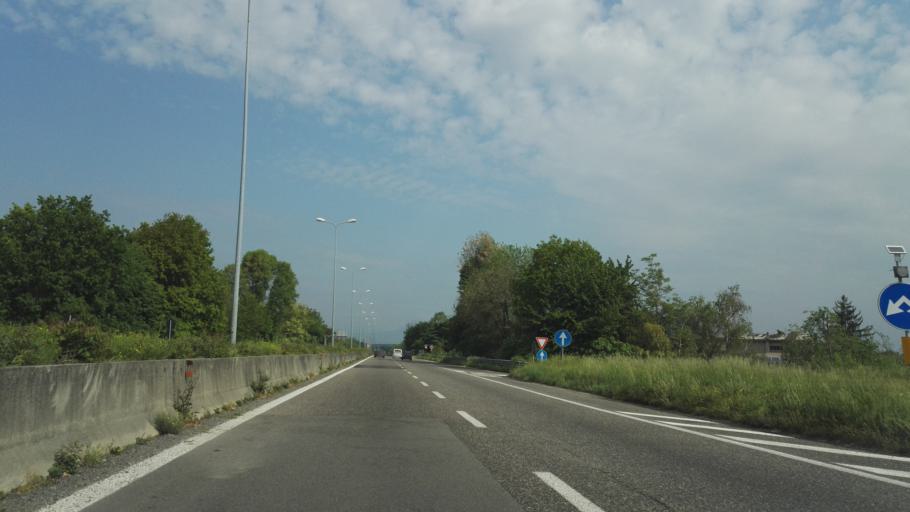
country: IT
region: Lombardy
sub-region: Provincia di Monza e Brianza
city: Cesano Maderno
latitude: 45.6377
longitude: 9.1593
